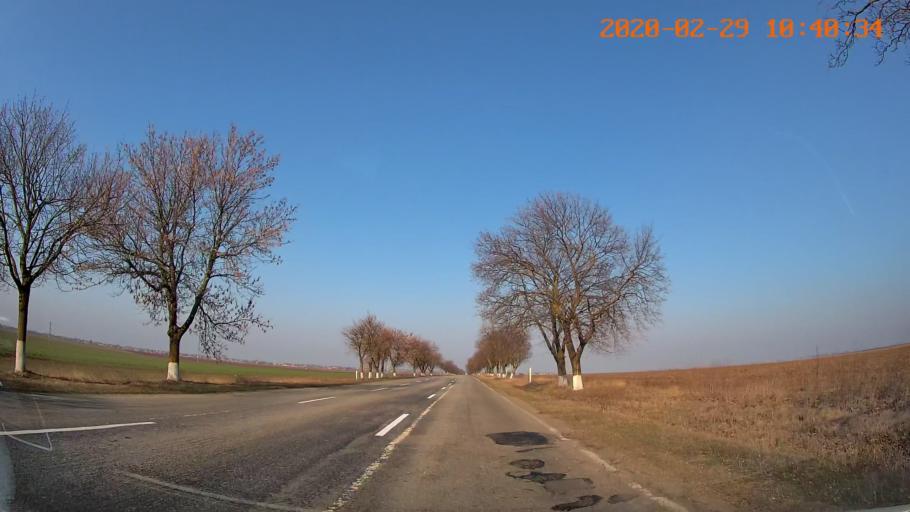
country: MD
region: Anenii Noi
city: Varnita
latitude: 47.0343
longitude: 29.4377
